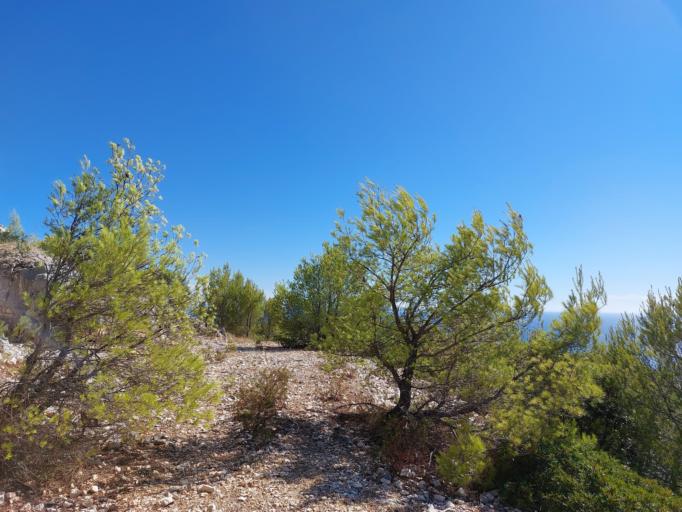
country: HR
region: Dubrovacko-Neretvanska
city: Smokvica
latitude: 42.7395
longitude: 16.8392
